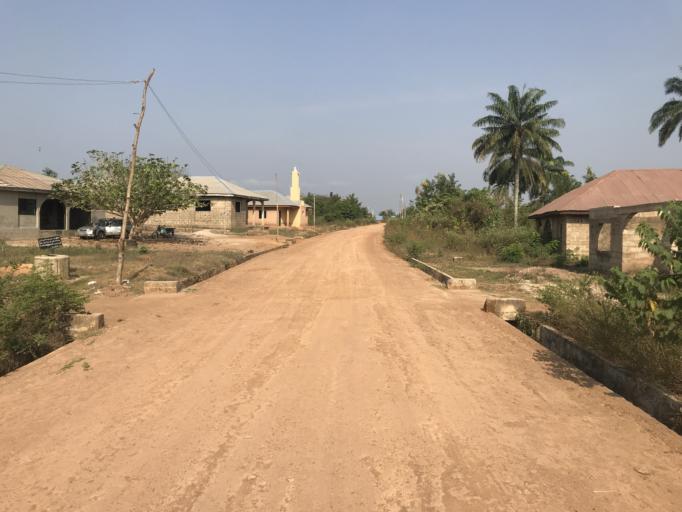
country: NG
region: Osun
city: Iwo
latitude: 7.6168
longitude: 4.1528
